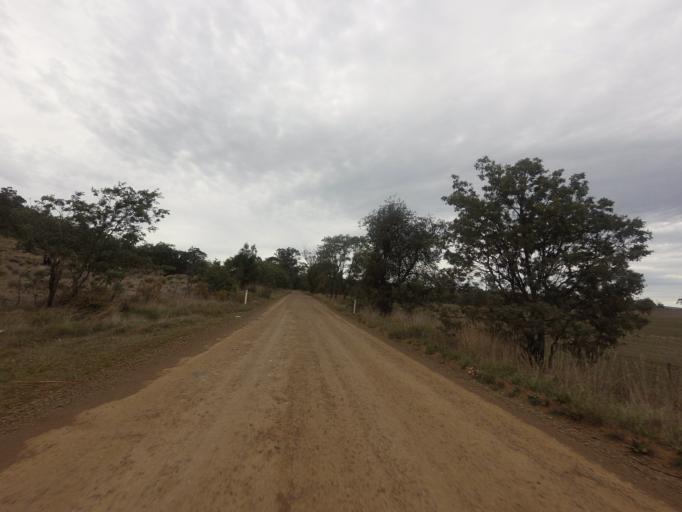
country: AU
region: Tasmania
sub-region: Derwent Valley
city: New Norfolk
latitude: -42.5637
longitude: 146.9321
